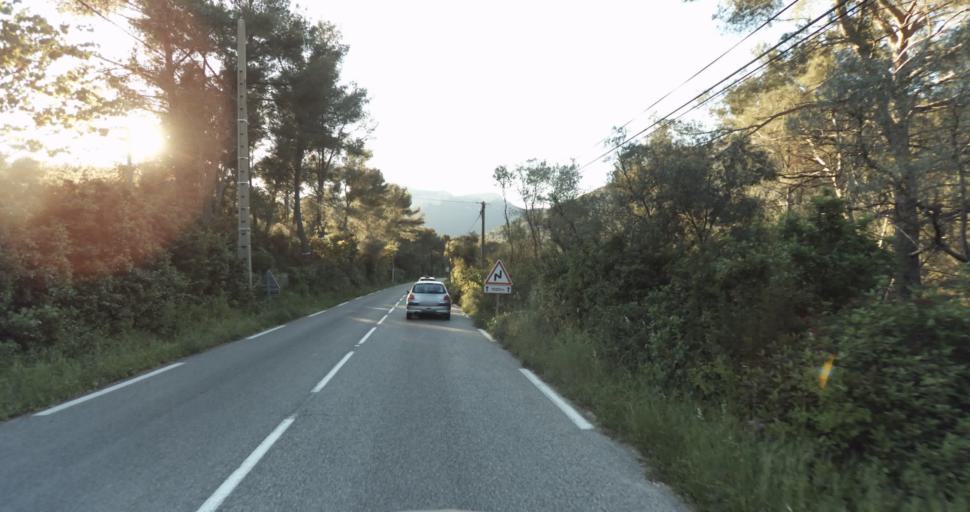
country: FR
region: Provence-Alpes-Cote d'Azur
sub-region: Departement du Var
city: Le Revest-les-Eaux
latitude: 43.1600
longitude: 5.9534
